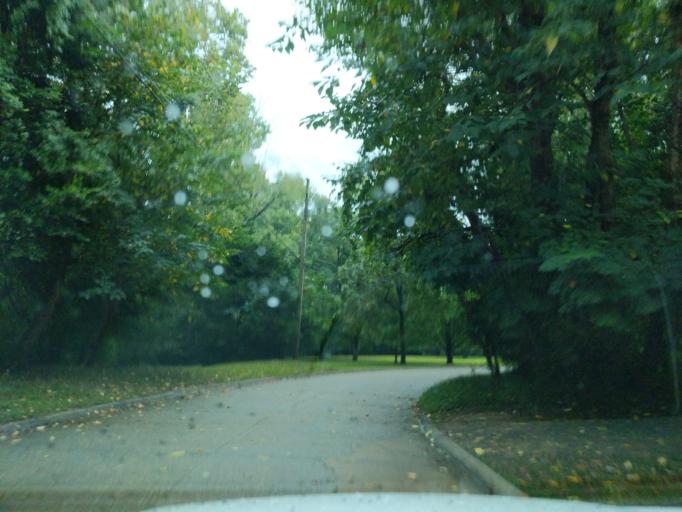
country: US
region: Mississippi
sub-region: Warren County
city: Vicksburg
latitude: 32.3671
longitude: -90.8709
